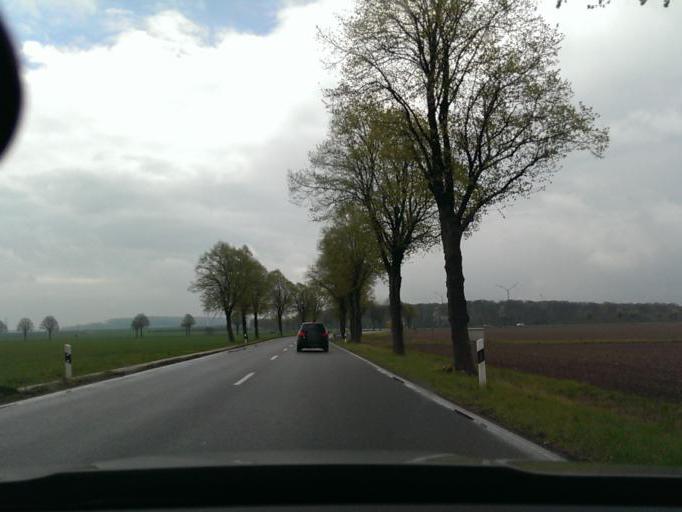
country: DE
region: Lower Saxony
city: Pattensen
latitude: 52.2131
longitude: 9.7464
